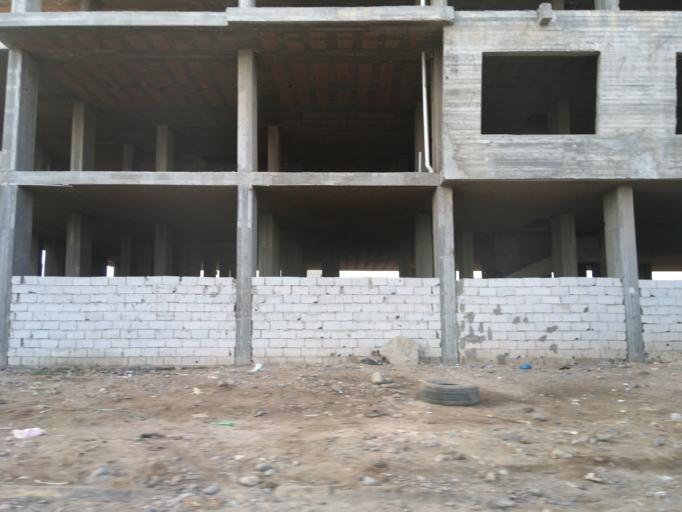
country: YE
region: Aden
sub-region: Ash Shaikh Outhman
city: Ash Shaykh `Uthman
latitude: 12.8588
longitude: 45.0050
